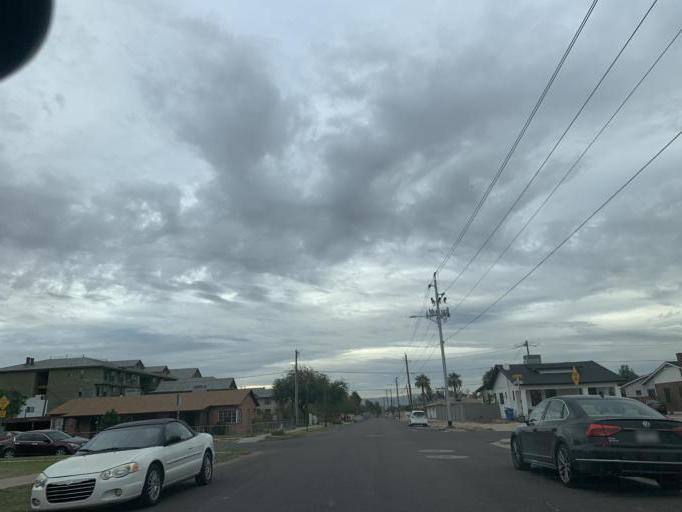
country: US
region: Arizona
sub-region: Maricopa County
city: Phoenix
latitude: 33.4650
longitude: -112.0520
